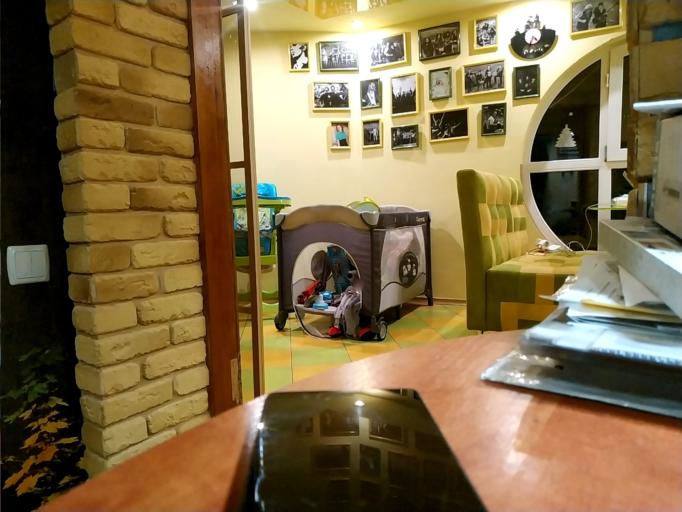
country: RU
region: Orjol
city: Naryshkino
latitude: 53.0018
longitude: 35.6966
